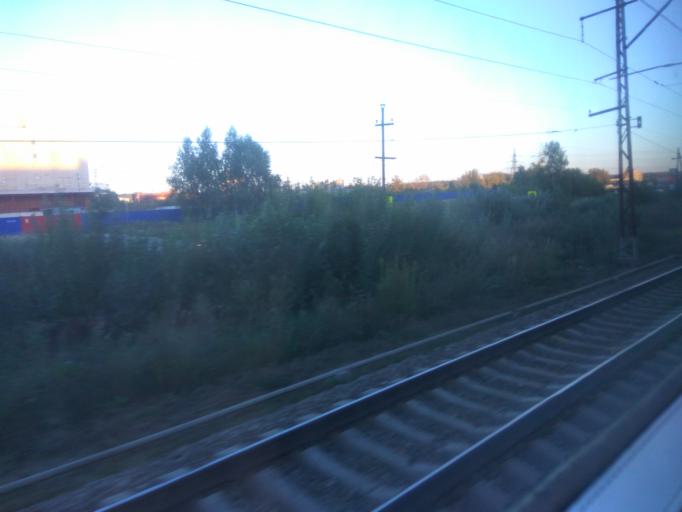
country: RU
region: Moskovskaya
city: Elektrostal'
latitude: 55.7798
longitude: 38.4639
